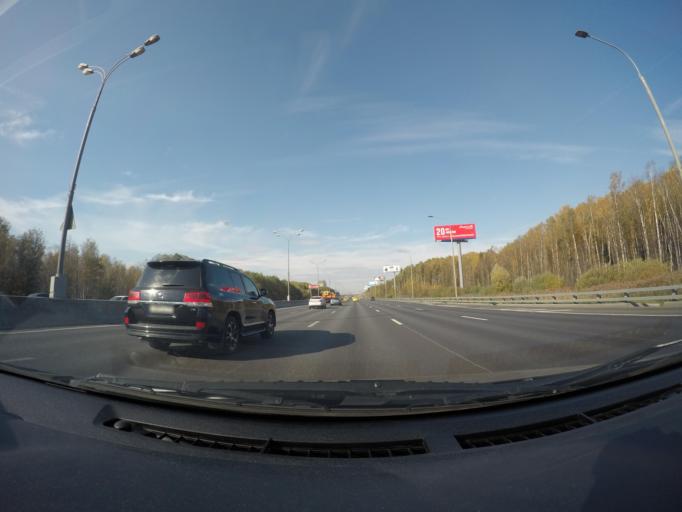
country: RU
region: Moskovskaya
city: Druzhba
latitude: 55.8721
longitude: 37.7463
